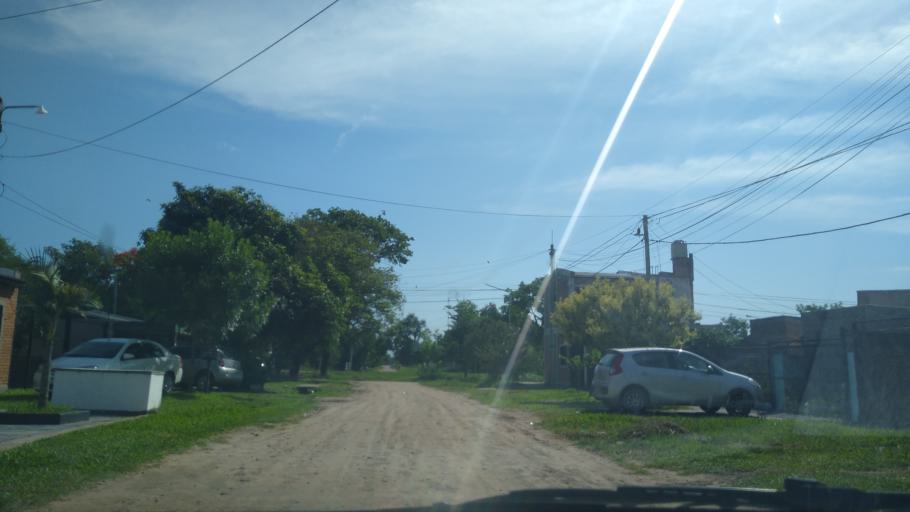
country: AR
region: Chaco
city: Barranqueras
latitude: -27.4874
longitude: -58.9533
